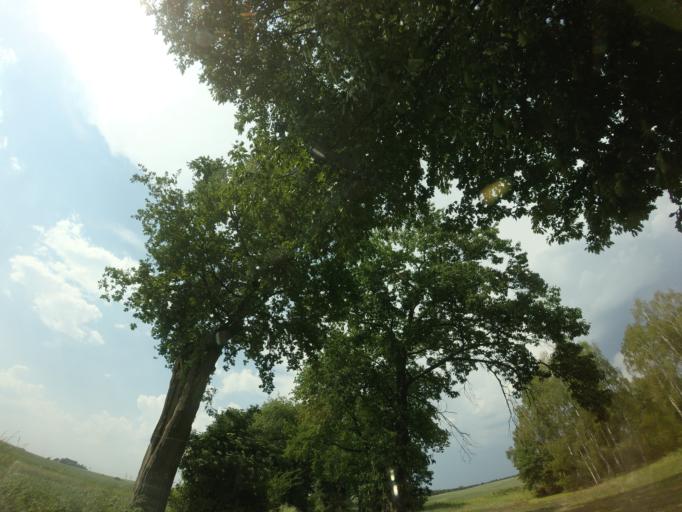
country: PL
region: West Pomeranian Voivodeship
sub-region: Powiat choszczenski
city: Krzecin
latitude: 53.1291
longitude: 15.5895
